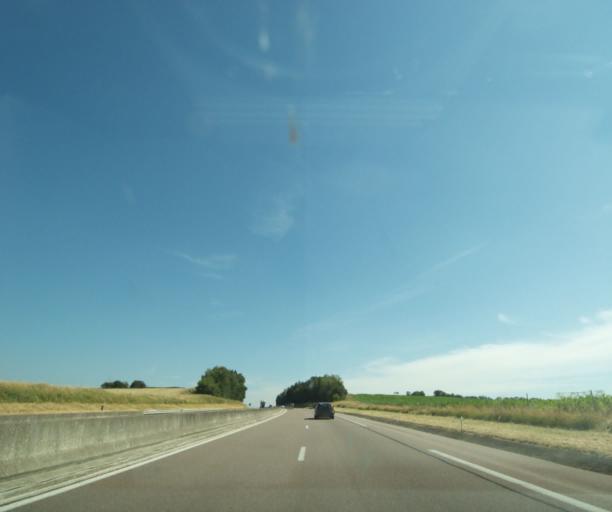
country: FR
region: Lorraine
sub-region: Departement des Vosges
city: Chatenois
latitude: 48.3767
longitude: 5.8808
